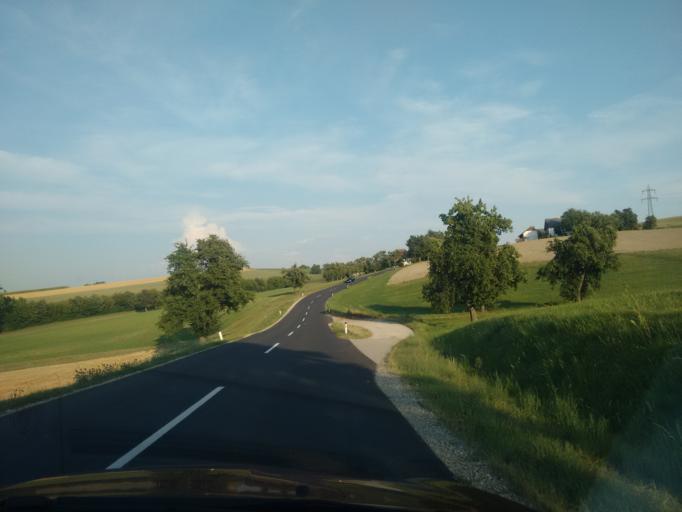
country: AT
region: Upper Austria
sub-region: Politischer Bezirk Vocklabruck
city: Wolfsegg am Hausruck
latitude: 48.1579
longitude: 13.6732
